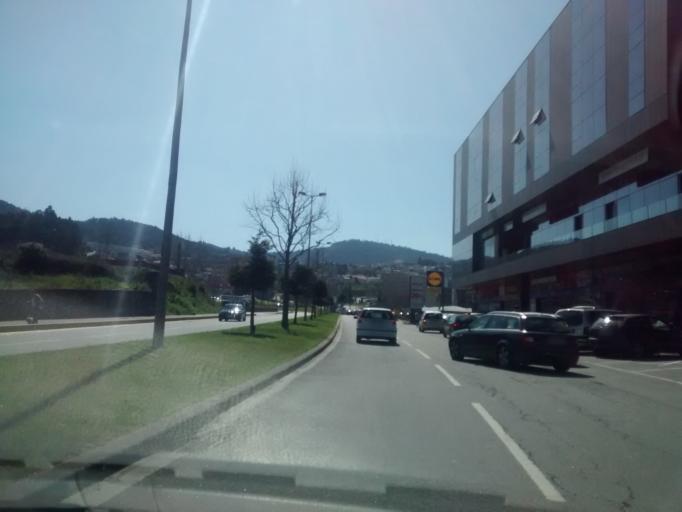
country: PT
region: Braga
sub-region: Braga
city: Braga
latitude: 41.5440
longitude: -8.3995
